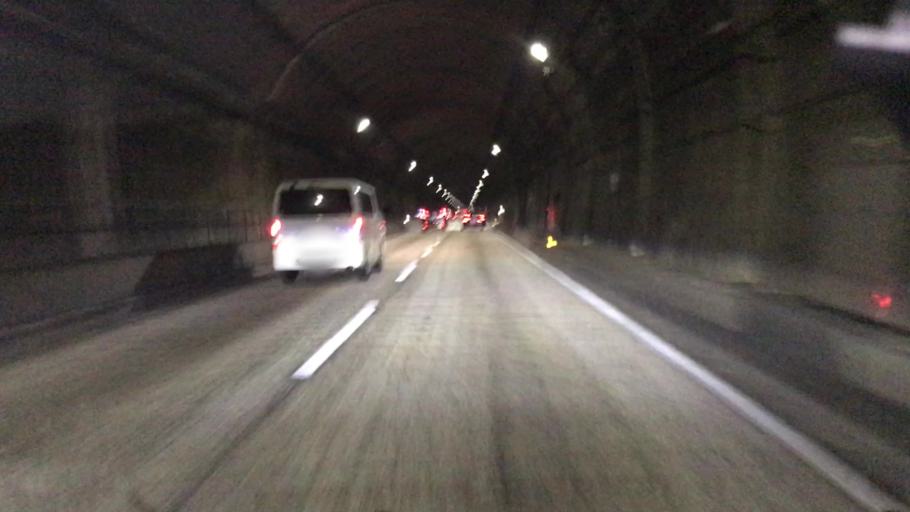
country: JP
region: Hyogo
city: Kobe
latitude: 34.7308
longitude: 135.1792
